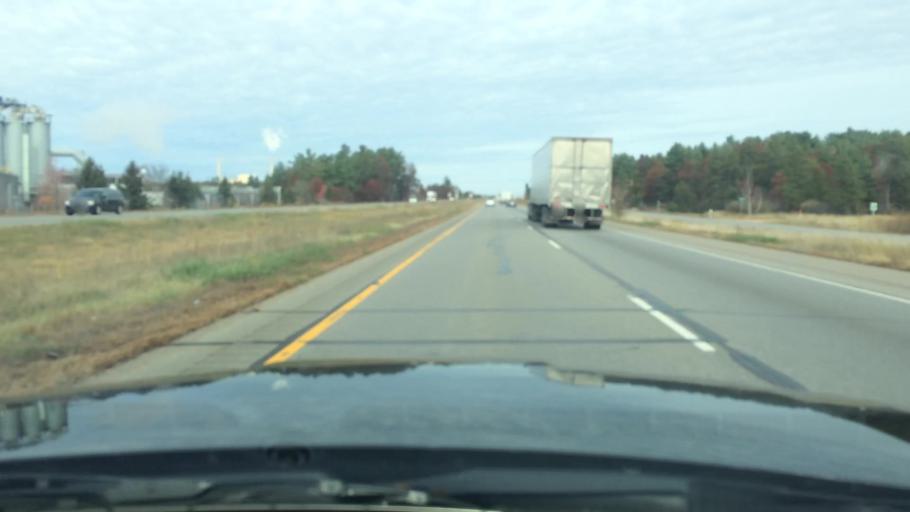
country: US
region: Wisconsin
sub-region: Marathon County
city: Evergreen
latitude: 44.8287
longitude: -89.6586
